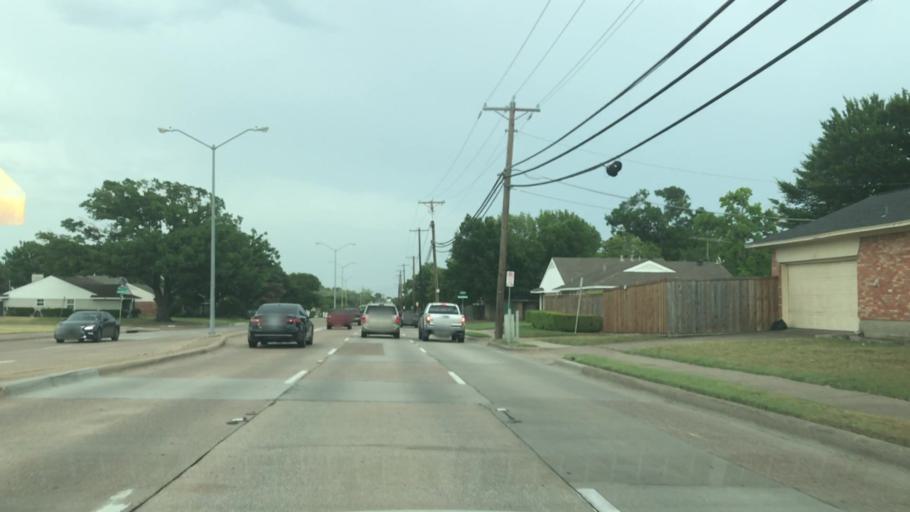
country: US
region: Texas
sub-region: Dallas County
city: Richardson
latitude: 32.8789
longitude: -96.7052
